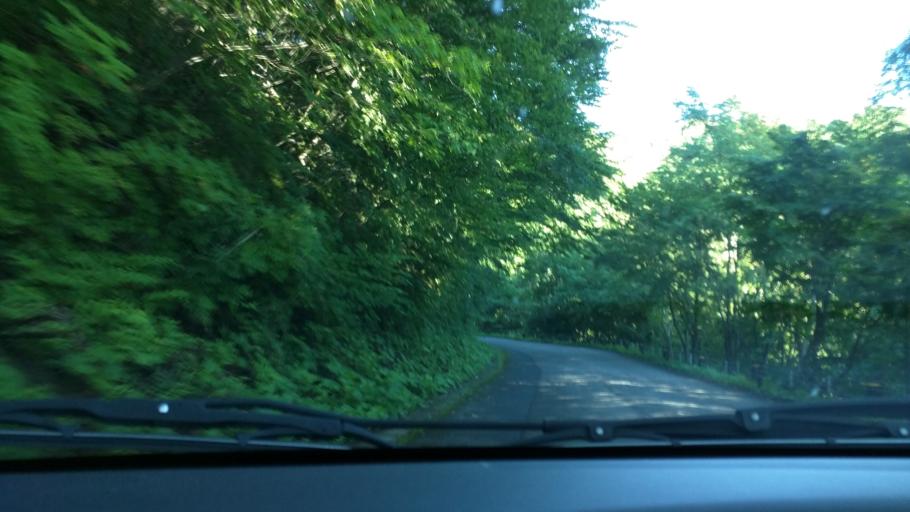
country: JP
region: Fukushima
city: Inawashiro
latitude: 37.3439
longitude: 140.0588
